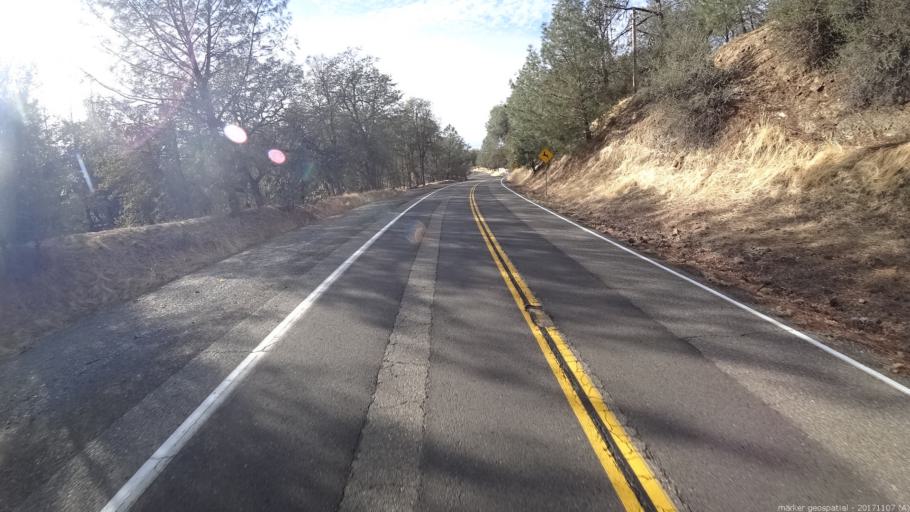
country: US
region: California
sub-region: Shasta County
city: Shasta
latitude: 40.5153
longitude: -122.5140
